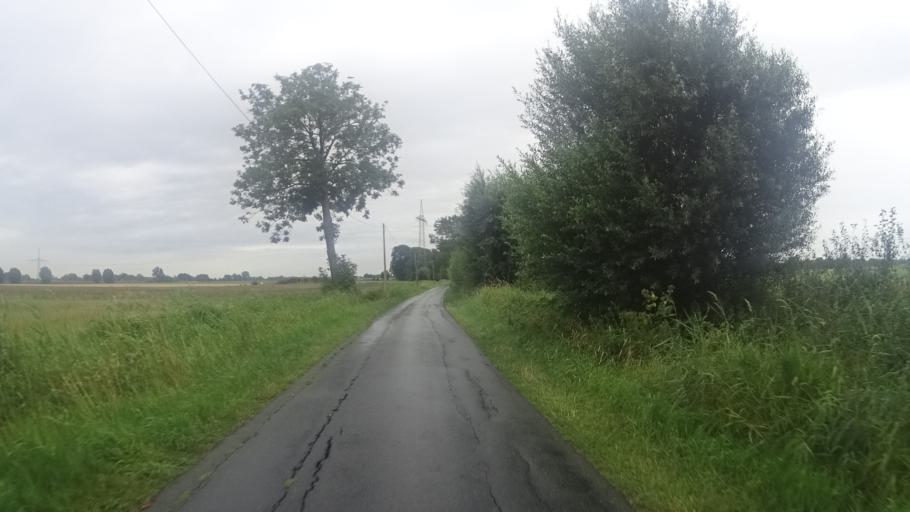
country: DE
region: Schleswig-Holstein
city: Sommerland
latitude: 53.7865
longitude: 9.5426
